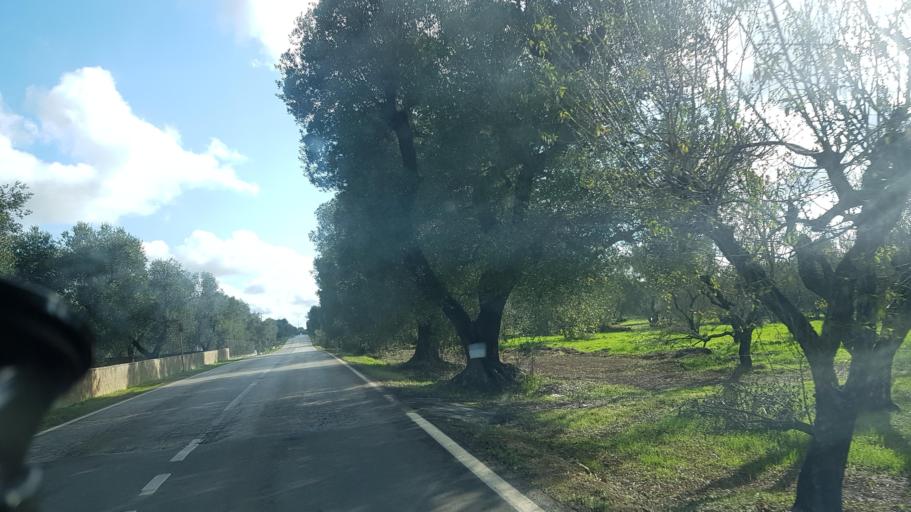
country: IT
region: Apulia
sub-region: Provincia di Brindisi
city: San Michele Salentino
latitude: 40.6524
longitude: 17.6052
